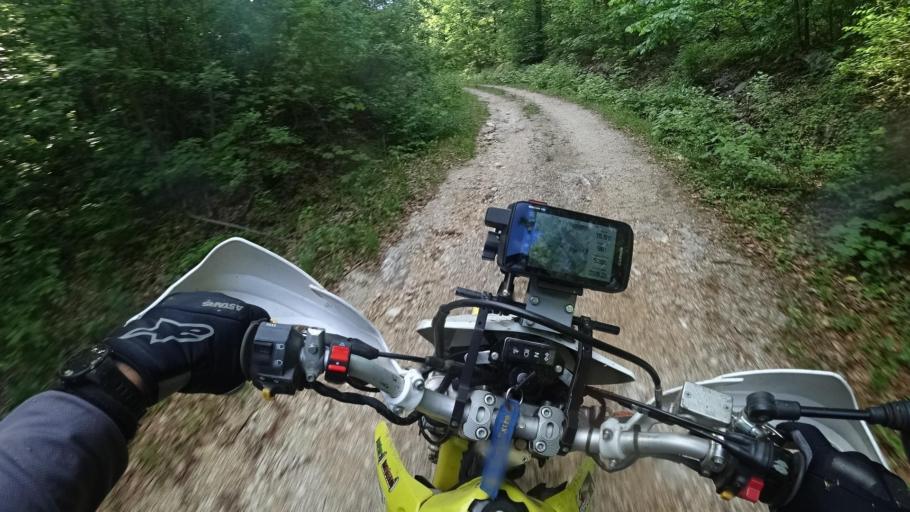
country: BA
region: Federation of Bosnia and Herzegovina
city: Sanica
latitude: 44.6552
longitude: 16.6113
